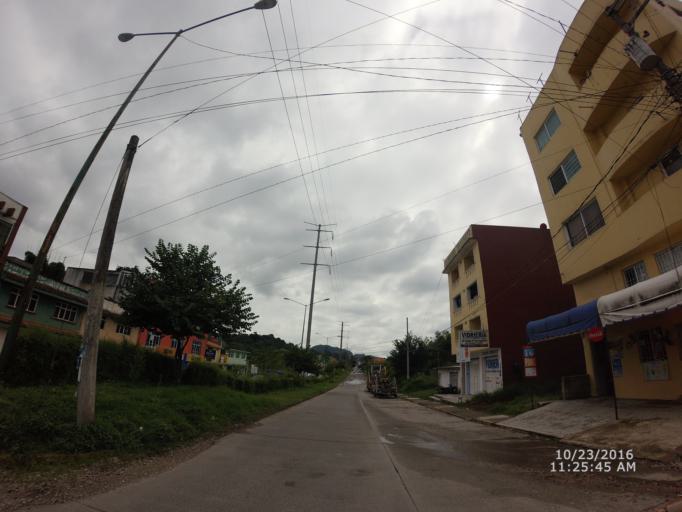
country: MX
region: Veracruz
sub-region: Tlalnelhuayocan
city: Guadalupe Victoria
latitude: 19.5509
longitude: -96.9445
